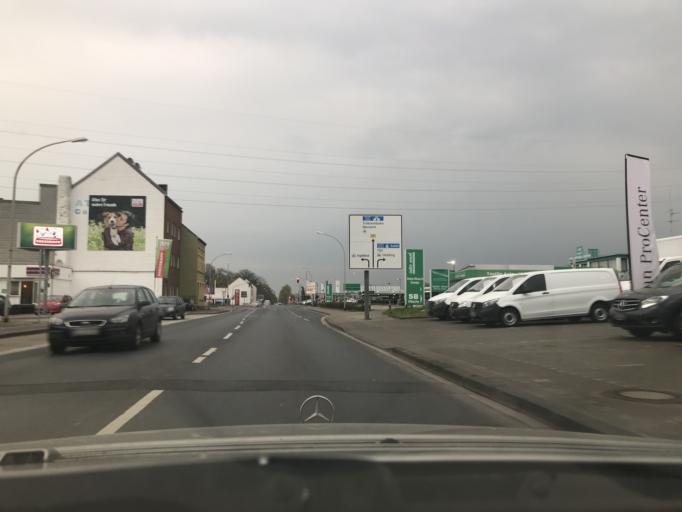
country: DE
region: North Rhine-Westphalia
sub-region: Regierungsbezirk Dusseldorf
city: Monchengladbach
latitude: 51.2095
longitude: 6.4640
